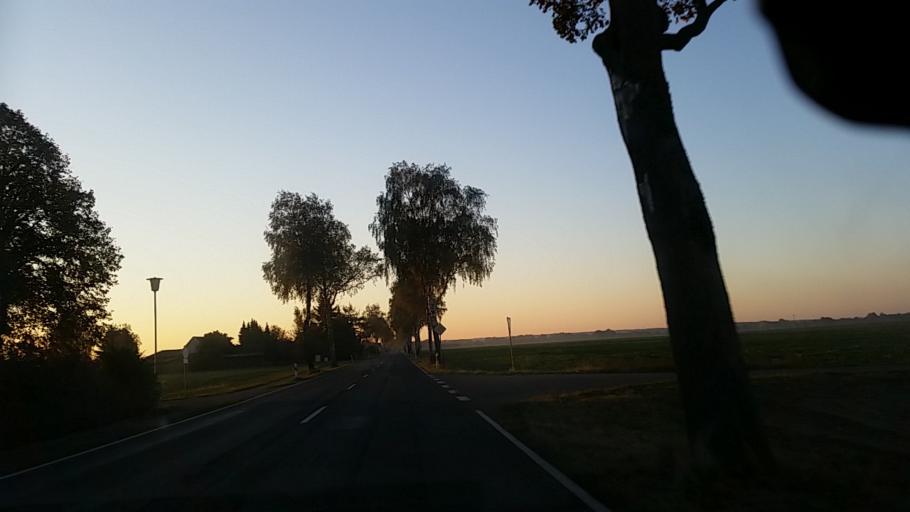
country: DE
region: Lower Saxony
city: Bodenteich
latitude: 52.8136
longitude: 10.6969
